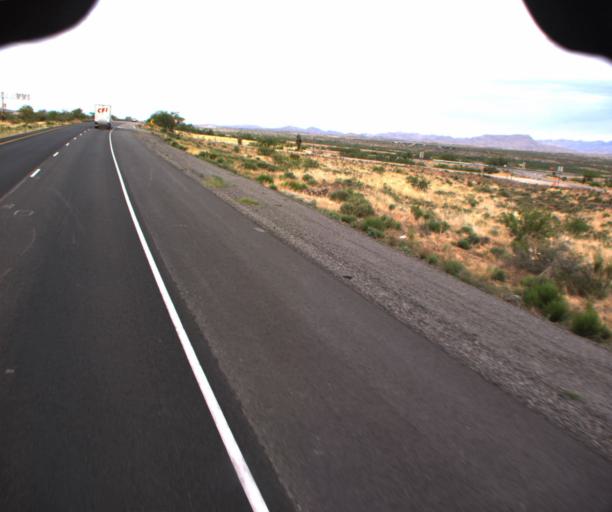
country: US
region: Arizona
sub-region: Cochise County
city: Mescal
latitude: 31.9761
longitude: -110.5093
